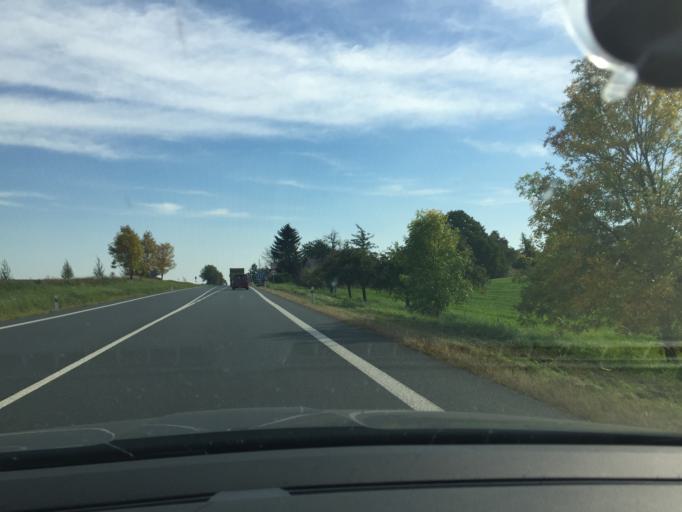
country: CZ
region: Central Bohemia
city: Velim
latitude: 50.0405
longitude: 15.1039
